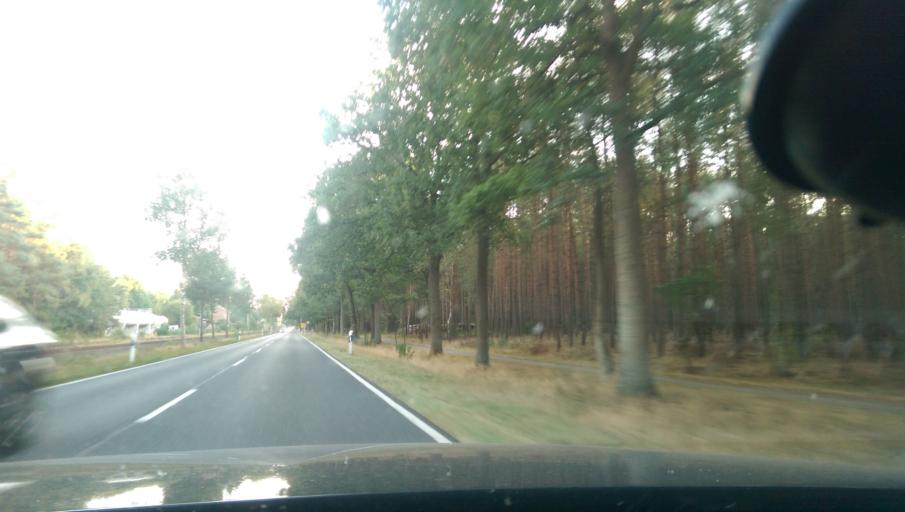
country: DE
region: Lower Saxony
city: Walsrode
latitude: 52.8152
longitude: 9.5936
